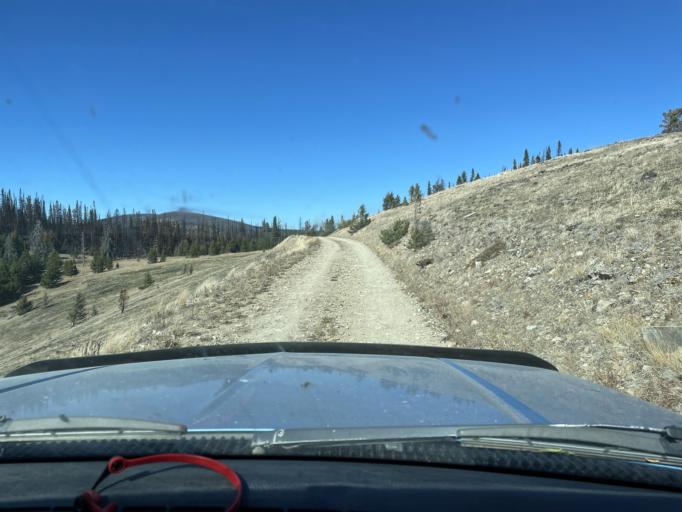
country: US
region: Montana
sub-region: Broadwater County
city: Townsend
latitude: 46.4971
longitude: -111.2576
